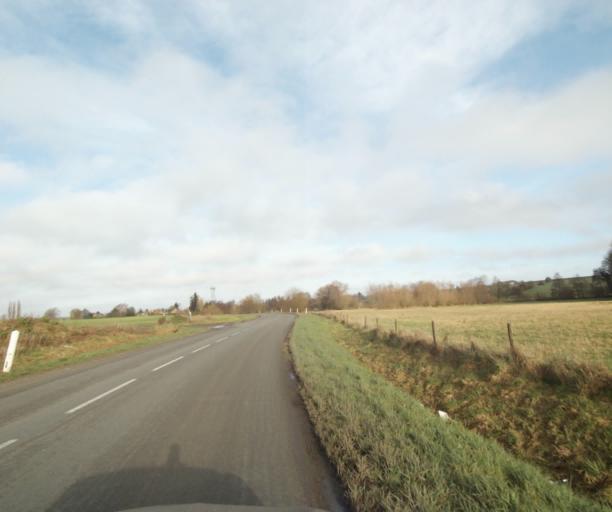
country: FR
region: Nord-Pas-de-Calais
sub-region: Departement du Nord
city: Thiant
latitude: 50.2773
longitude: 3.4535
